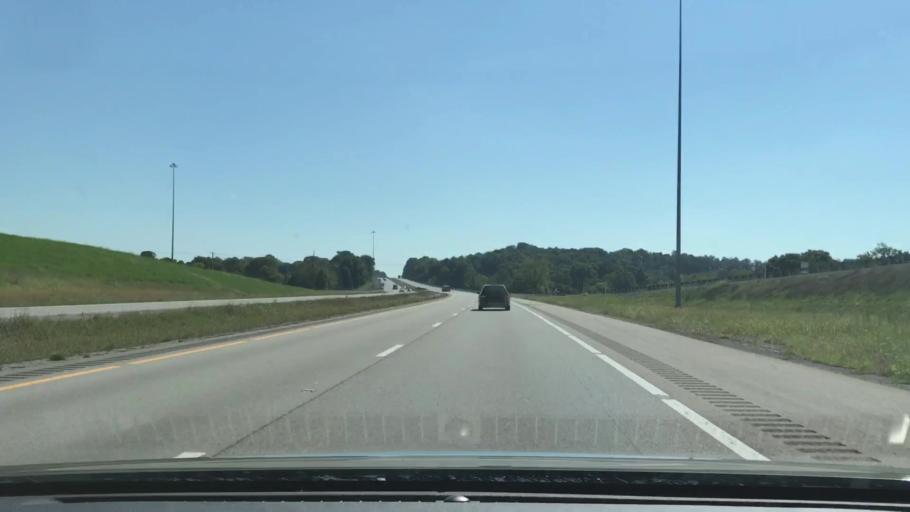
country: US
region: Kentucky
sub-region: Barren County
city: Glasgow
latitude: 36.9917
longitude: -85.9809
